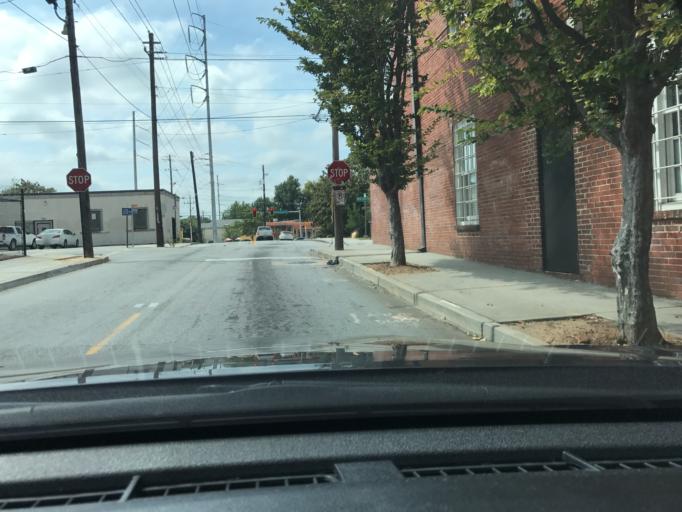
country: US
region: Georgia
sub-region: Fulton County
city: Atlanta
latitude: 33.7477
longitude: -84.3767
